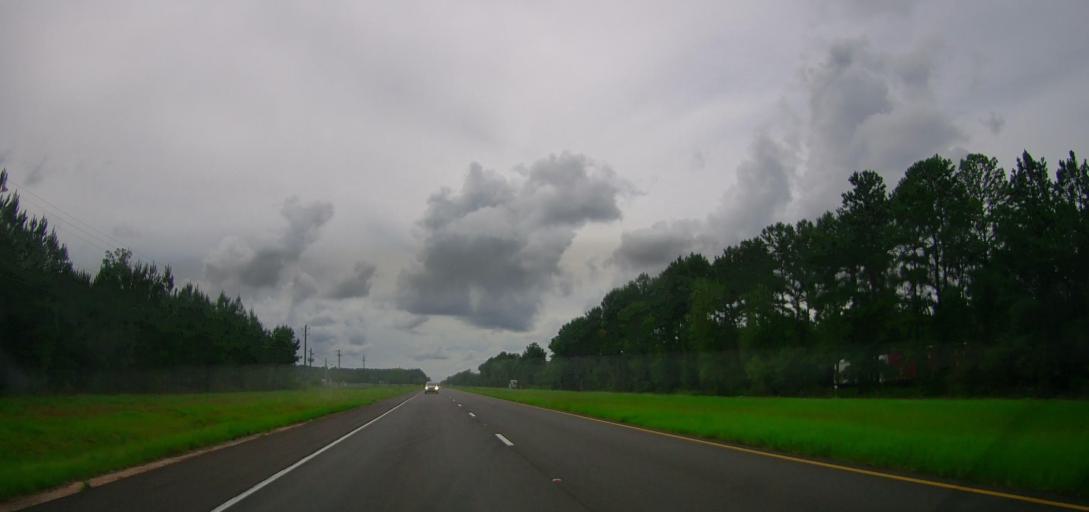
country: US
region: Georgia
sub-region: Wayne County
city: Jesup
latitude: 31.6430
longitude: -81.9651
